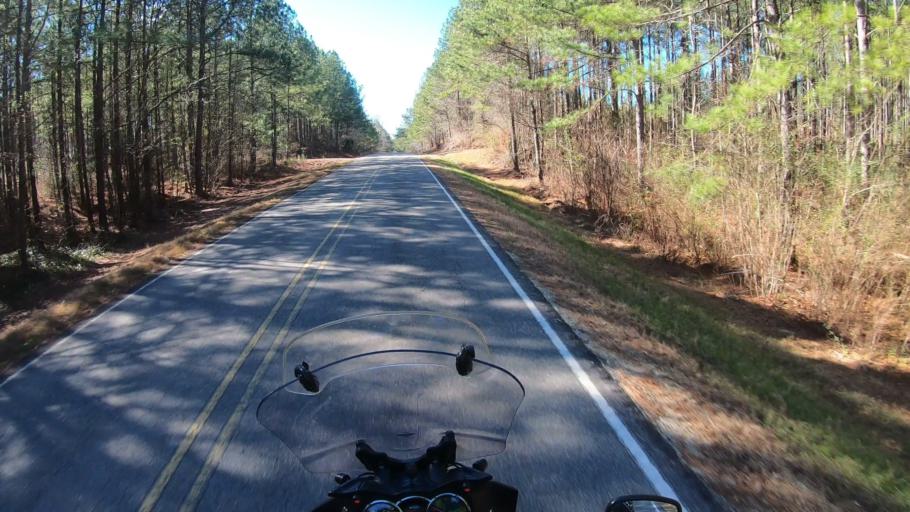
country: US
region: Alabama
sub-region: Clay County
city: Ashland
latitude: 33.3711
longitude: -85.8906
